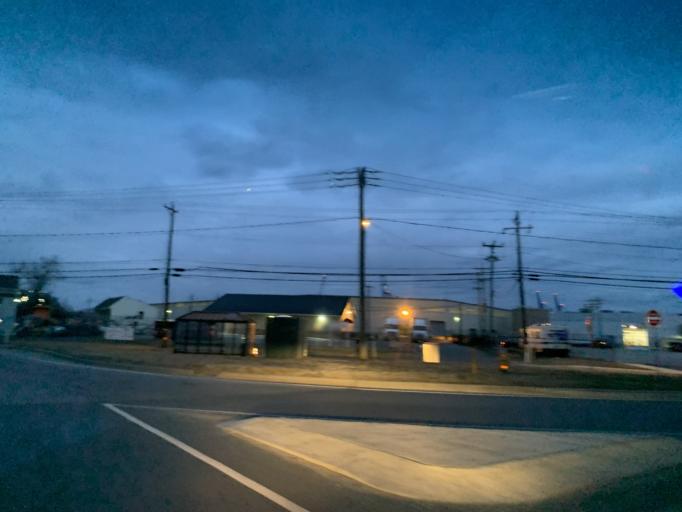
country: US
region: Delaware
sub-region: New Castle County
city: Wilmington
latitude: 39.7167
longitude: -75.5327
